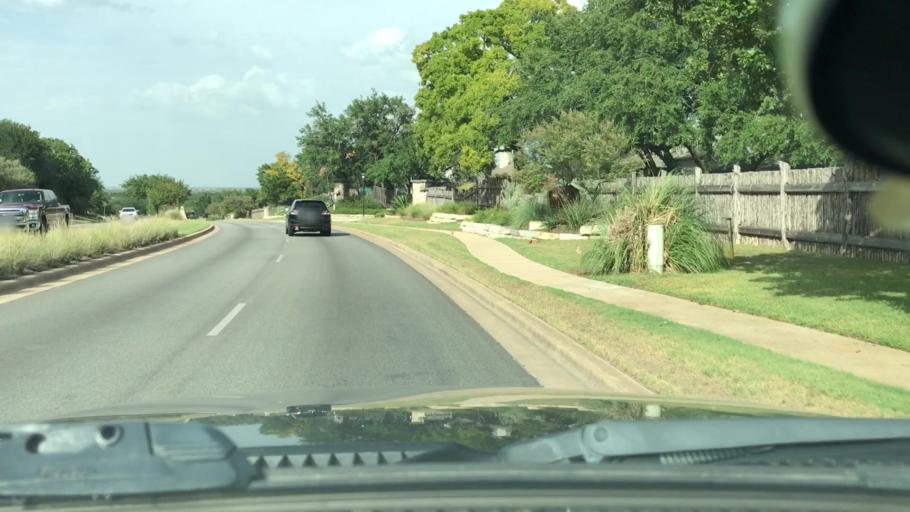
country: US
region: Texas
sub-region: Williamson County
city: Leander
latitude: 30.5472
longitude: -97.8587
